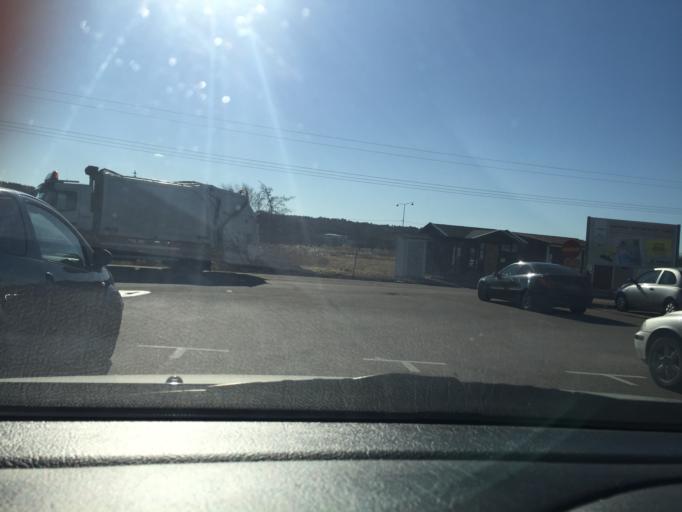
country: SE
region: Vaestra Goetaland
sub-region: Molndal
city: Moelndal
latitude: 57.6468
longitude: 11.9671
